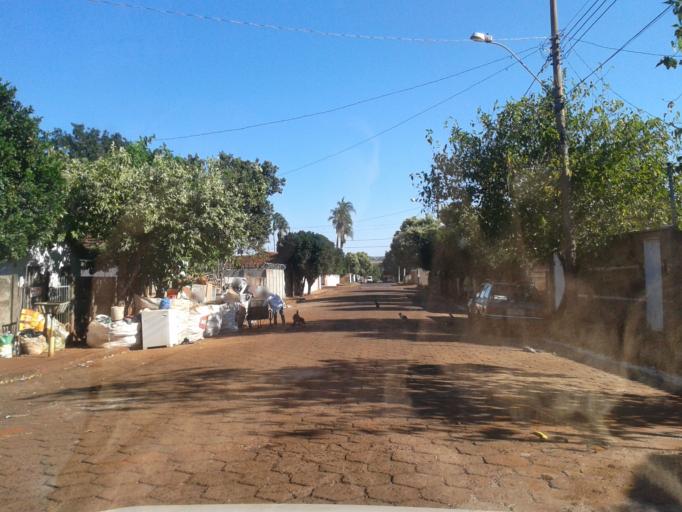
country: BR
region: Minas Gerais
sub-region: Centralina
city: Centralina
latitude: -18.7196
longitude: -49.2043
